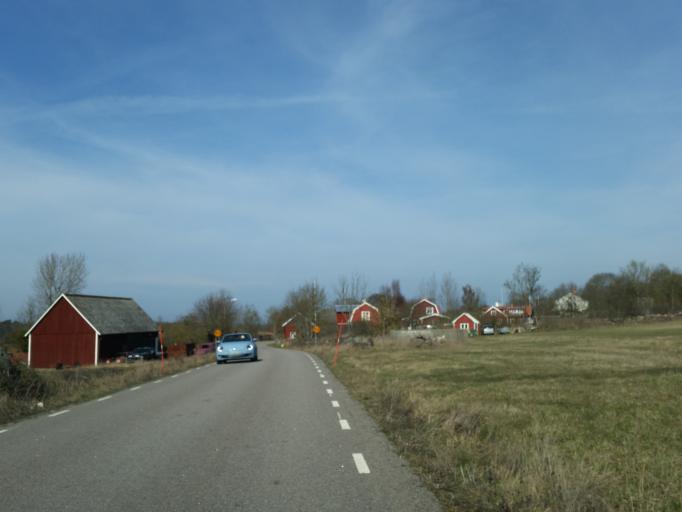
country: SE
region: Kalmar
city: Faerjestaden
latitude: 56.7351
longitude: 16.5419
